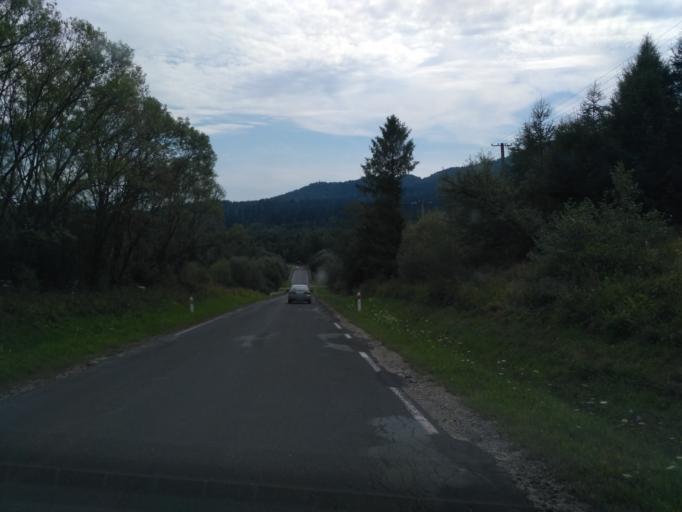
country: PL
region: Subcarpathian Voivodeship
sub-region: Powiat bieszczadzki
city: Lutowiska
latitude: 49.2033
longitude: 22.6757
